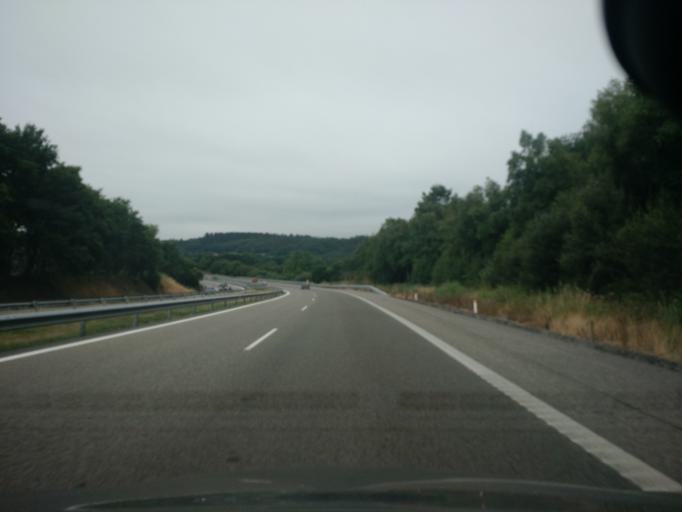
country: ES
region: Galicia
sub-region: Provincia da Coruna
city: Oroso
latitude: 42.9726
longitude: -8.4486
